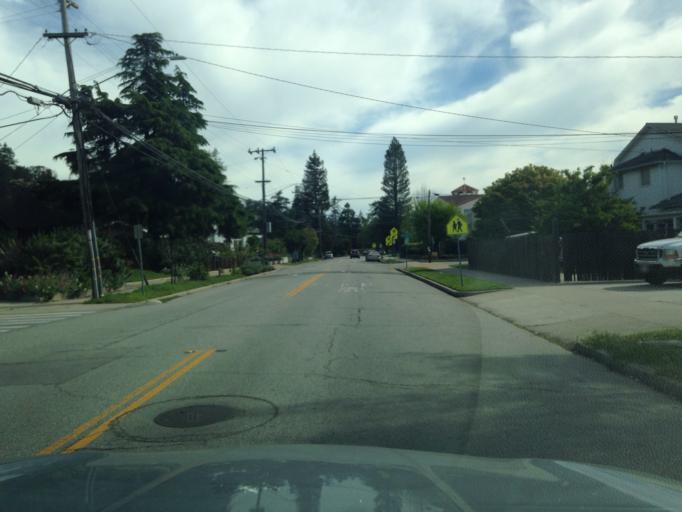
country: US
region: California
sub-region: Santa Cruz County
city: Santa Cruz
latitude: 36.9735
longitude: -122.0378
